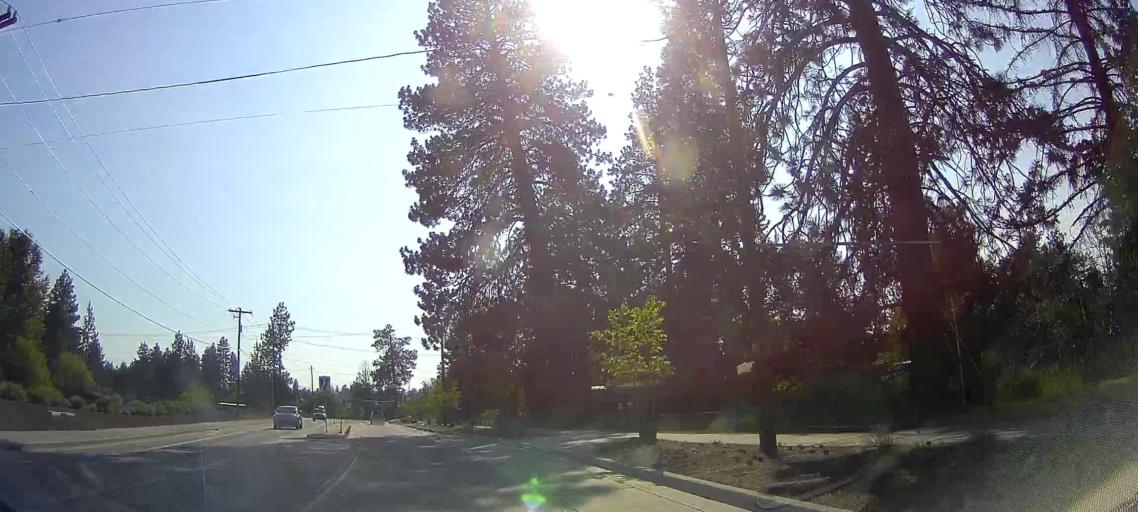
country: US
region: Oregon
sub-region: Deschutes County
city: Bend
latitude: 44.0387
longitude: -121.2991
